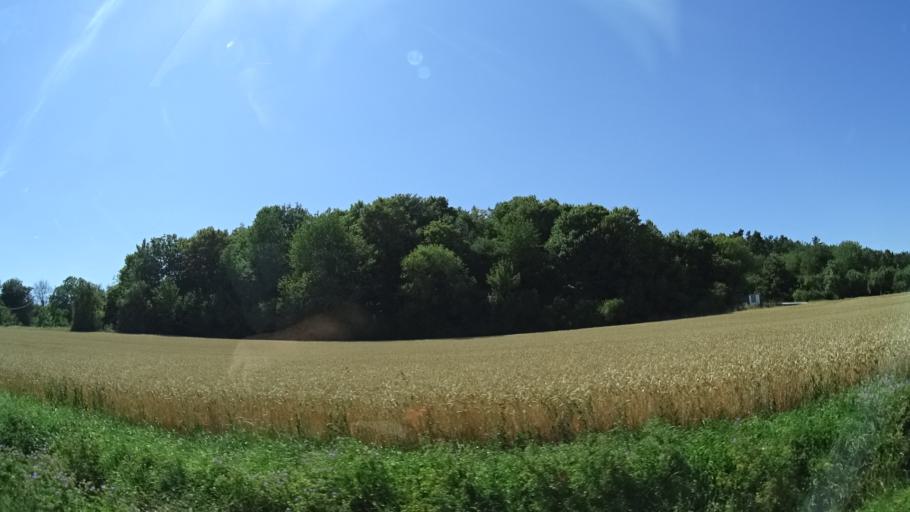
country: DE
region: Bavaria
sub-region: Regierungsbezirk Unterfranken
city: Helmstadt
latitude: 49.7514
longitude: 9.7087
